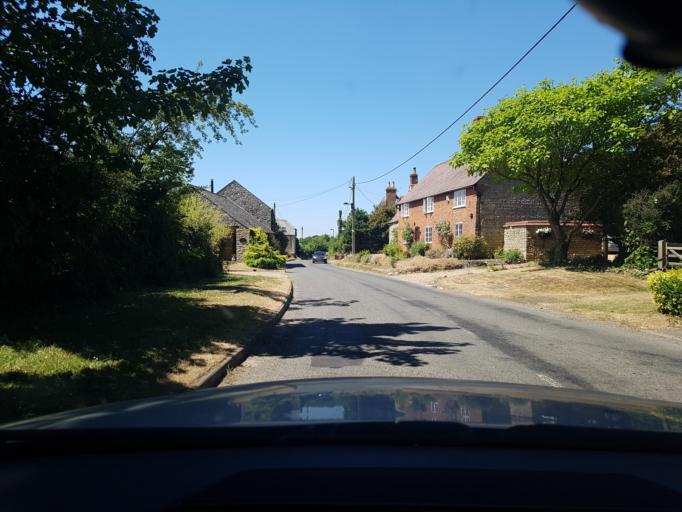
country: GB
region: England
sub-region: Milton Keynes
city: Calverton
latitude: 52.0322
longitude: -0.8335
